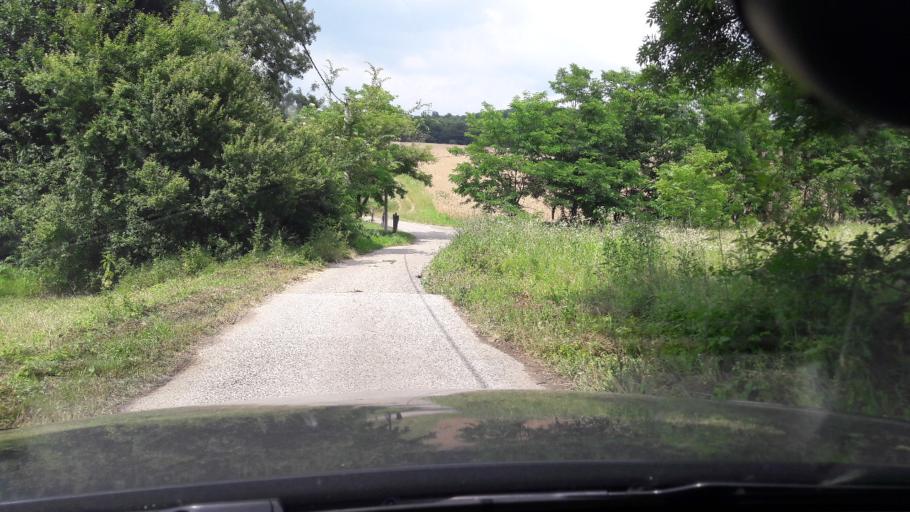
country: RS
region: Central Serbia
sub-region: Belgrade
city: Sopot
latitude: 44.6262
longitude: 20.5999
